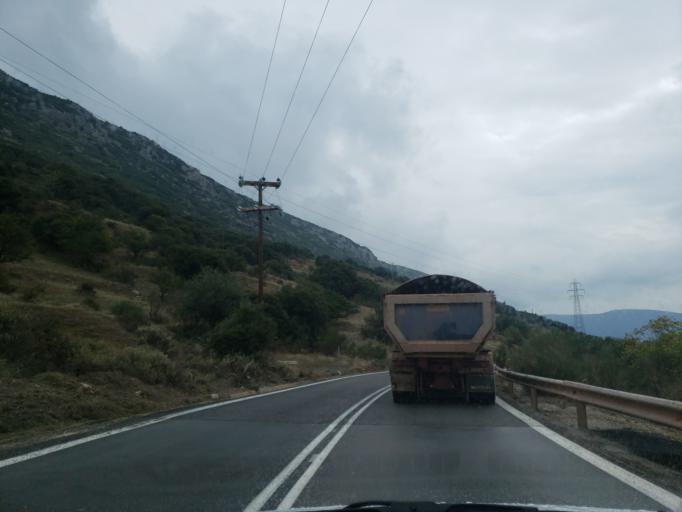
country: GR
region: Central Greece
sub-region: Nomos Fokidos
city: Amfissa
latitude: 38.5693
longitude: 22.3975
